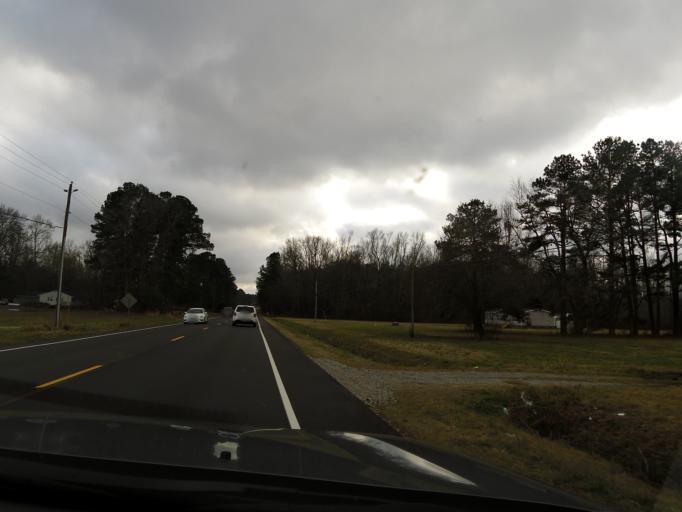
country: US
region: North Carolina
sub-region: Nash County
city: Rocky Mount
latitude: 35.9023
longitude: -77.7402
